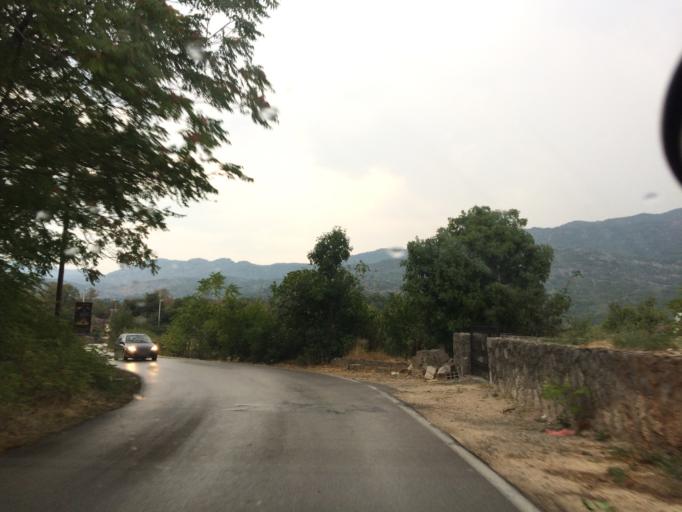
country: ME
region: Opstina Niksic
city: Niksic
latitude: 42.6809
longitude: 18.9785
